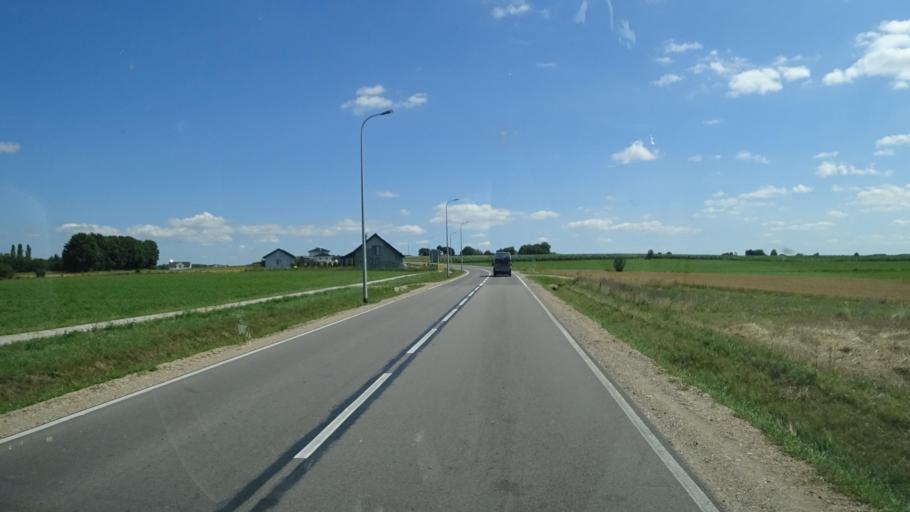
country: PL
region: Podlasie
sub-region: Powiat lomzynski
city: Piatnica
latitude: 53.2485
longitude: 22.1101
